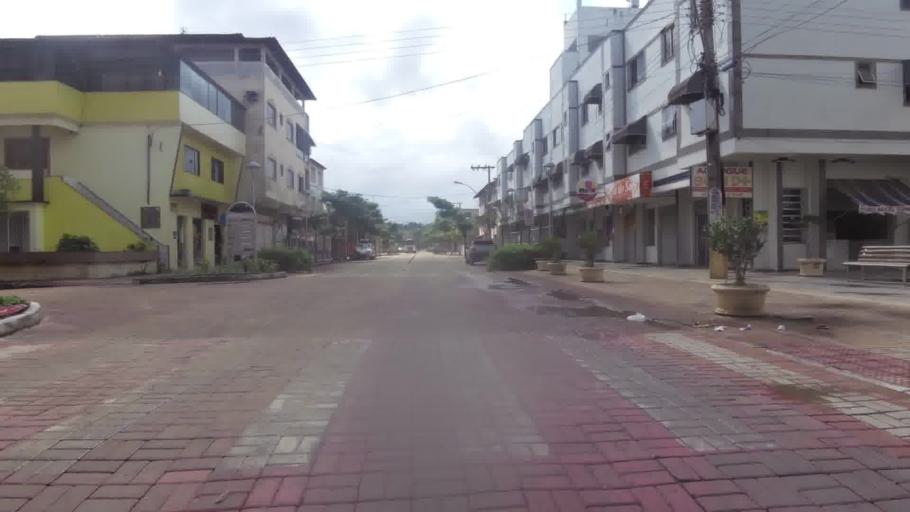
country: BR
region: Espirito Santo
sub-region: Piuma
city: Piuma
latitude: -20.8305
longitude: -40.6940
